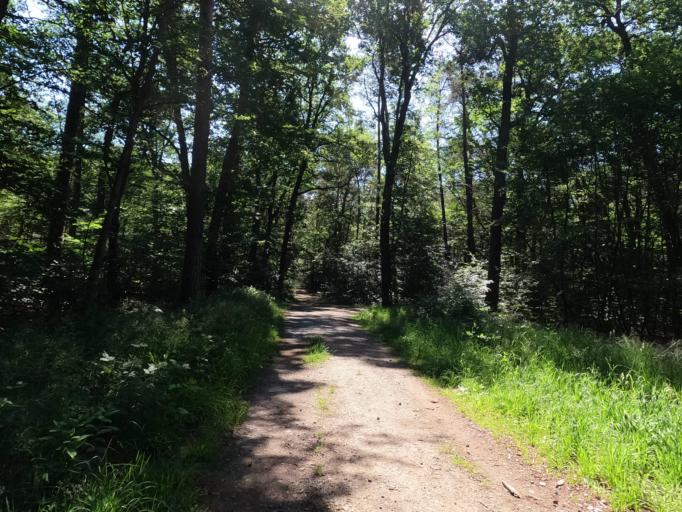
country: DE
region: Hesse
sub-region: Regierungsbezirk Darmstadt
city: Offenbach
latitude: 50.0681
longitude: 8.7415
